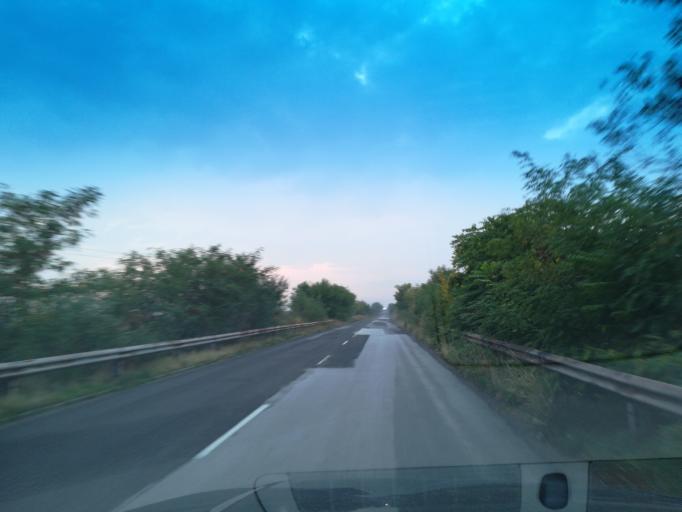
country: BG
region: Stara Zagora
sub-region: Obshtina Chirpan
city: Chirpan
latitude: 42.1945
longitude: 25.3047
